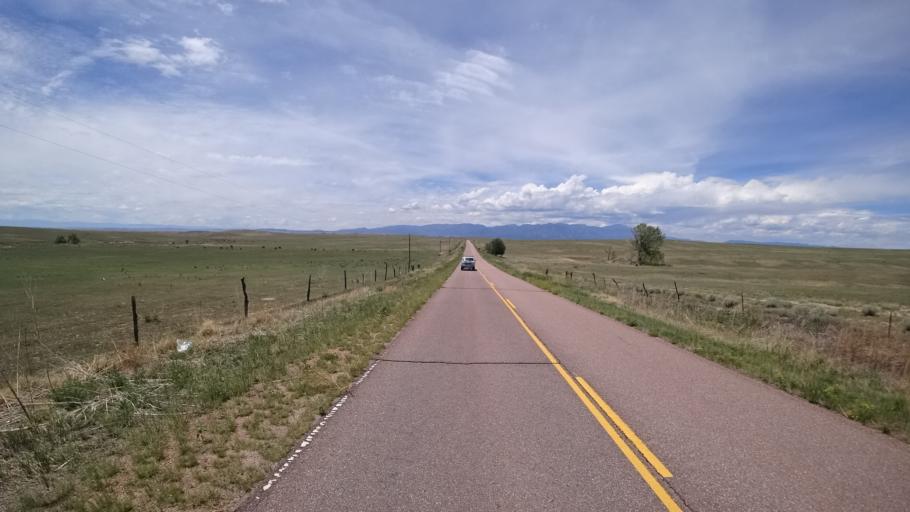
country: US
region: Colorado
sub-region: El Paso County
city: Fountain
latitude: 38.6940
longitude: -104.6002
